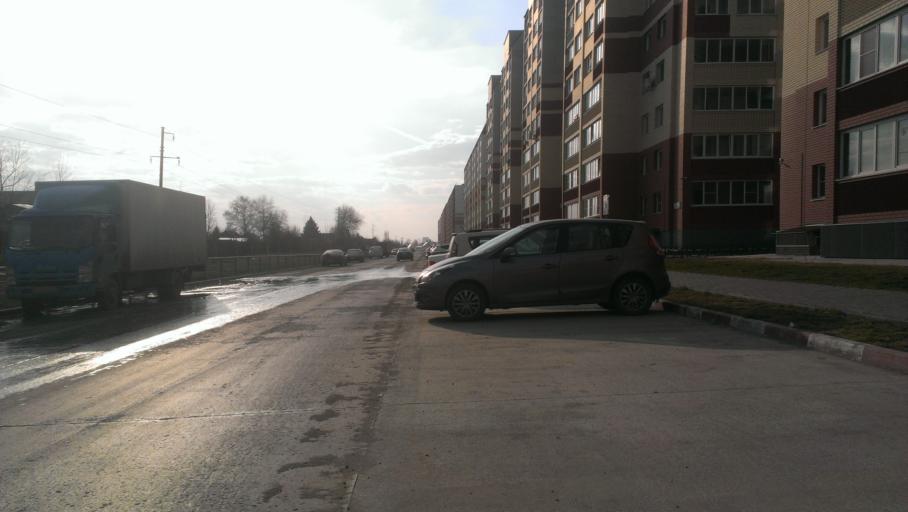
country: RU
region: Altai Krai
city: Novosilikatnyy
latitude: 53.3249
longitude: 83.6795
